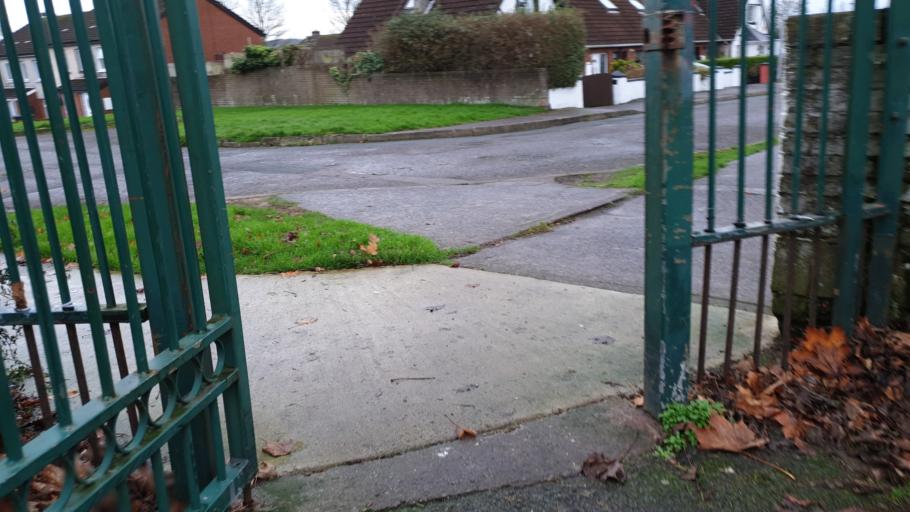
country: IE
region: Munster
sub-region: County Cork
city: Passage West
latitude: 51.8930
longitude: -8.3979
